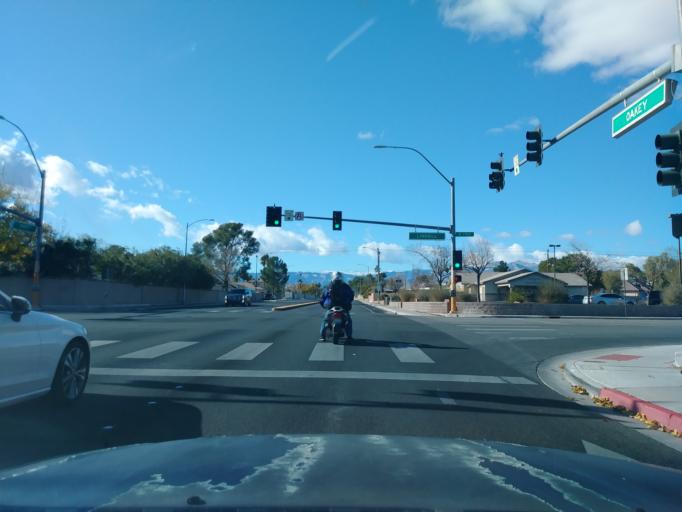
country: US
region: Nevada
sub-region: Clark County
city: Spring Valley
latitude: 36.1518
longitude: -115.2166
